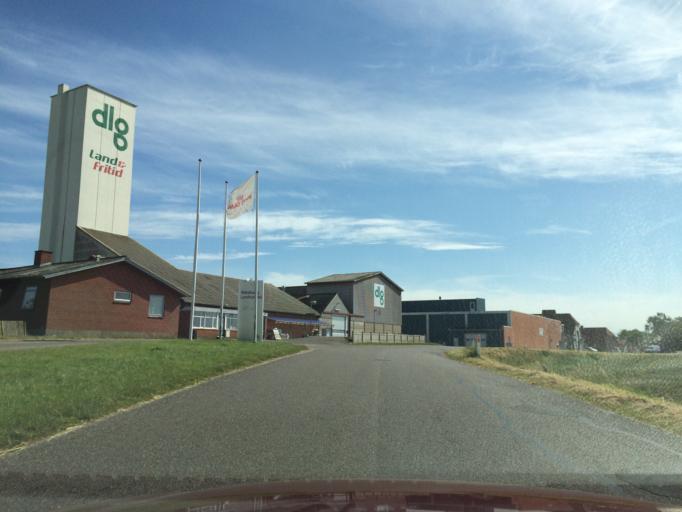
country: DK
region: Central Jutland
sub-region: Silkeborg Kommune
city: Silkeborg
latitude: 56.2210
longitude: 9.5615
